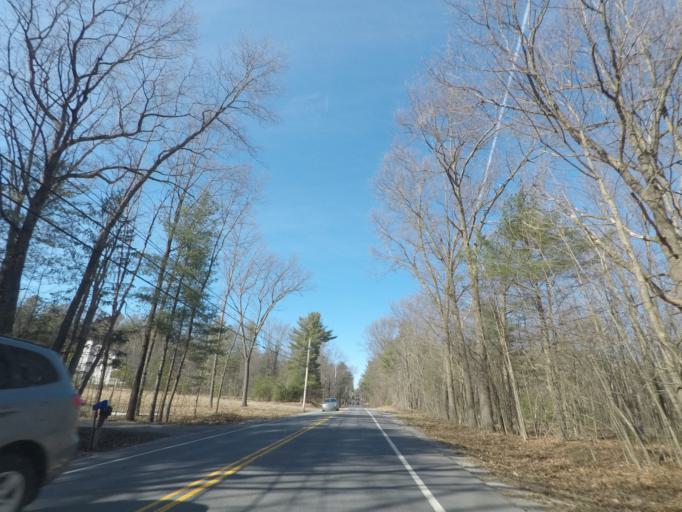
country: US
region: New York
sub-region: Saratoga County
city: North Ballston Spa
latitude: 43.0184
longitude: -73.8488
